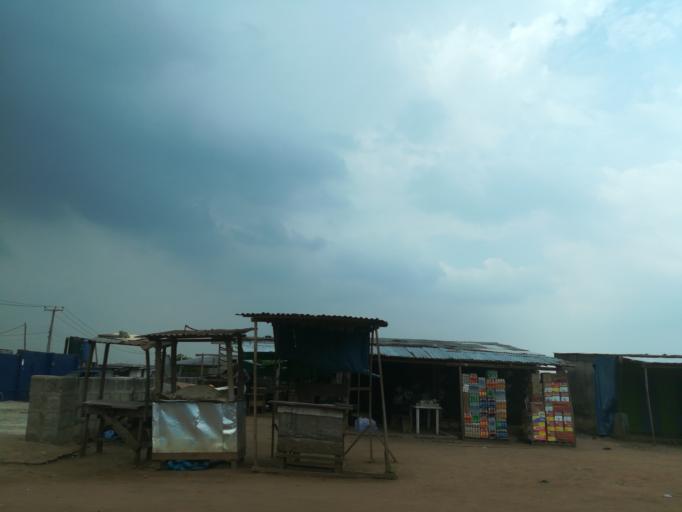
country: NG
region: Lagos
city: Ikorodu
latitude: 6.6036
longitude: 3.5869
